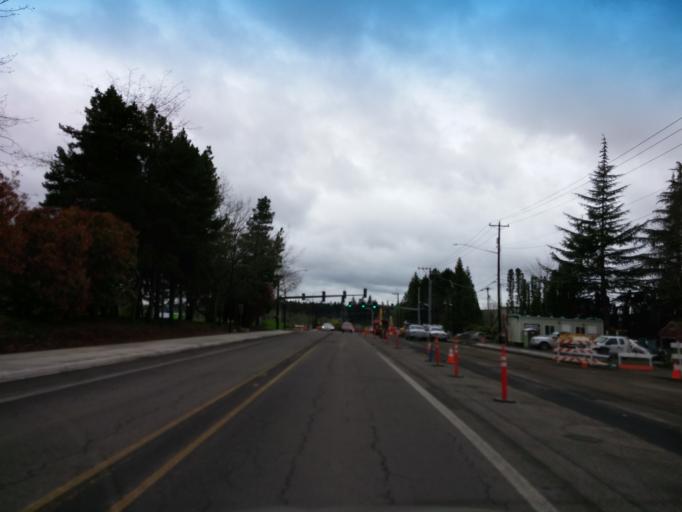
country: US
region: Oregon
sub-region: Washington County
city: Oak Hills
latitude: 45.5108
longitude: -122.8398
